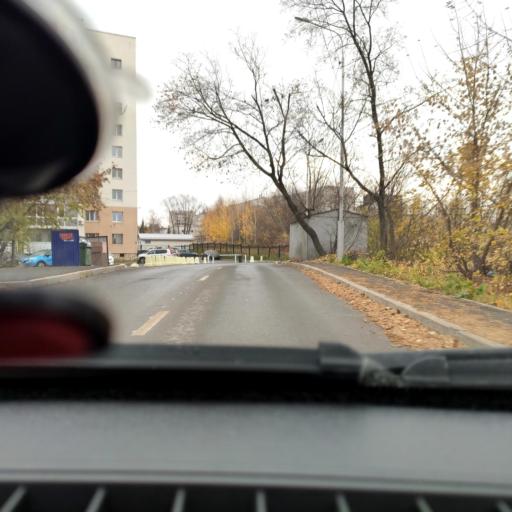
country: RU
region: Bashkortostan
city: Ufa
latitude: 54.7818
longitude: 56.0165
